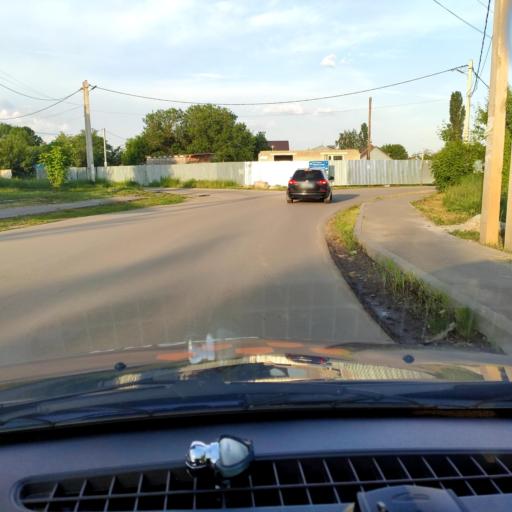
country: RU
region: Voronezj
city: Ramon'
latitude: 51.8278
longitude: 39.2678
